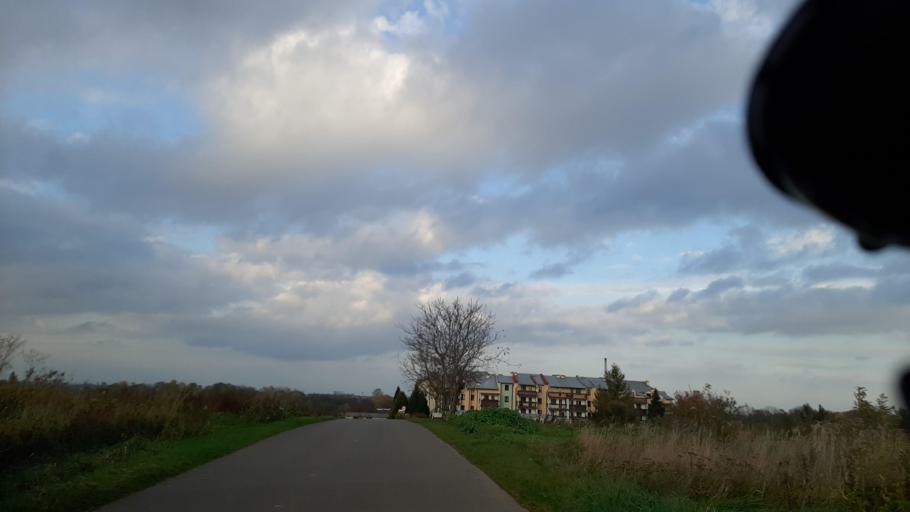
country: PL
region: Lublin Voivodeship
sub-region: Powiat lubelski
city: Garbow
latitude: 51.3461
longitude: 22.3294
